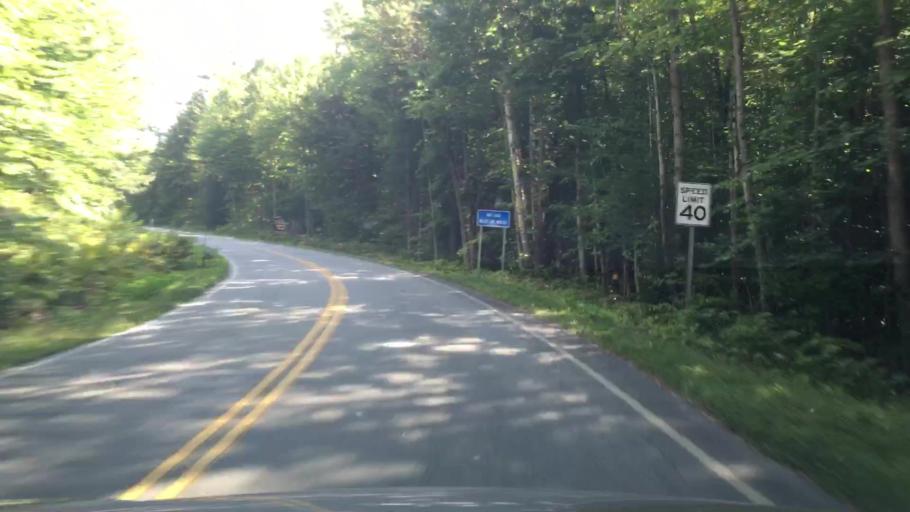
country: US
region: New Hampshire
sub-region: Carroll County
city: North Conway
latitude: 44.0697
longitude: -71.2830
